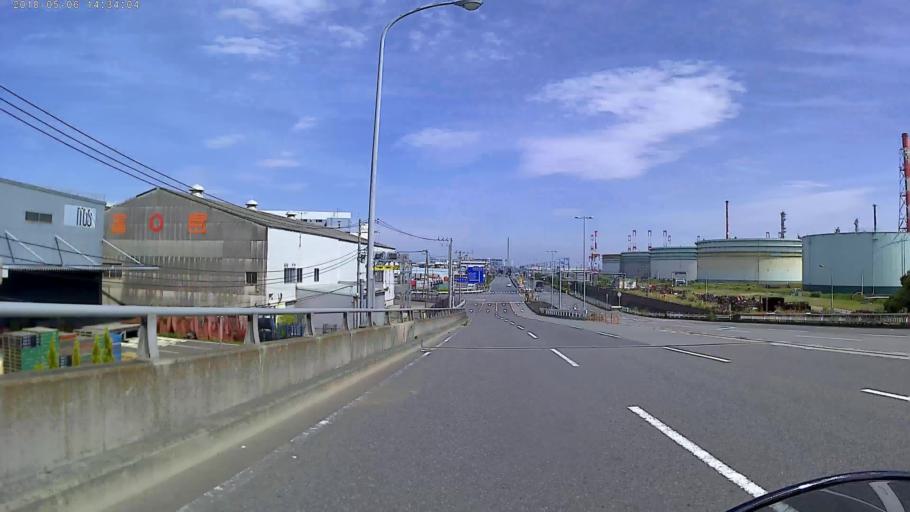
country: JP
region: Kanagawa
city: Yokohama
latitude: 35.4150
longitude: 139.6693
